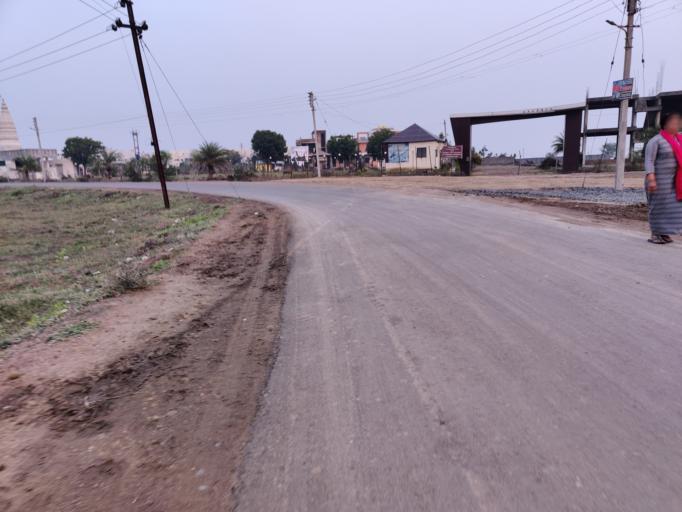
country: IN
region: Maharashtra
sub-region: Nagpur Division
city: Kamthi
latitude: 21.1957
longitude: 79.1528
